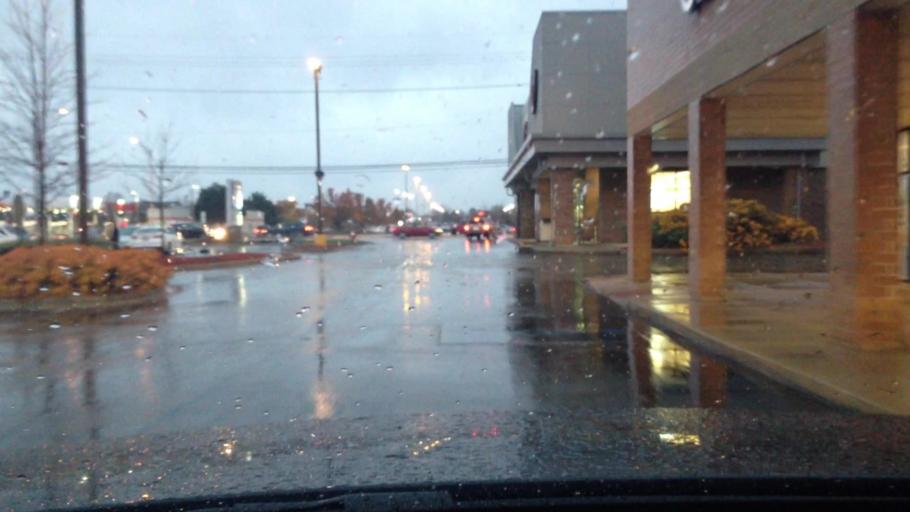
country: US
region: Illinois
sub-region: McHenry County
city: Lake in the Hills
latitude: 42.1765
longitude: -88.3367
